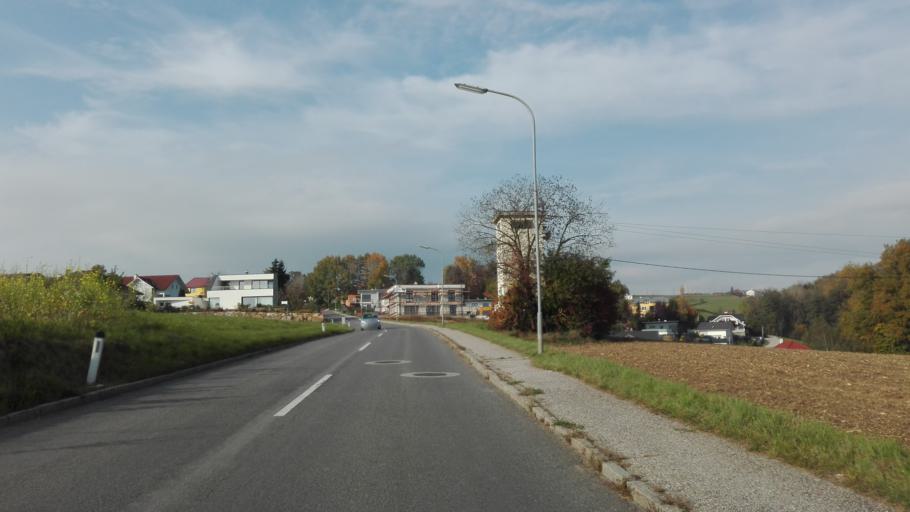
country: AT
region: Upper Austria
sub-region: Politischer Bezirk Perg
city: Perg
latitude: 48.2557
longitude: 14.6263
